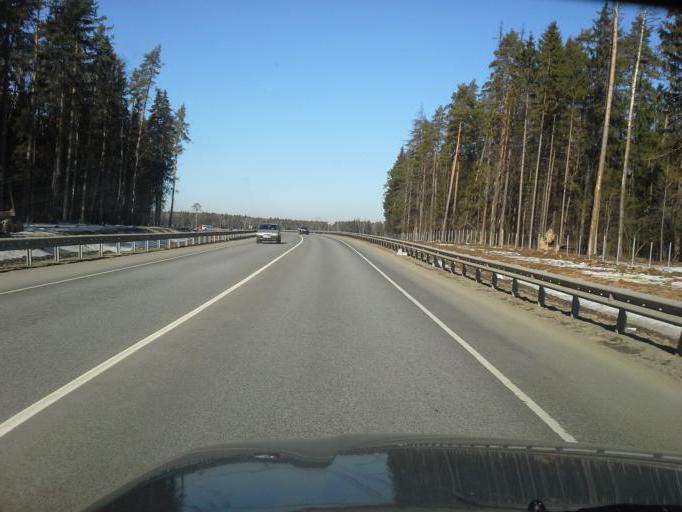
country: RU
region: Moskovskaya
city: Gorki Vtoryye
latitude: 55.6759
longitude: 37.1684
